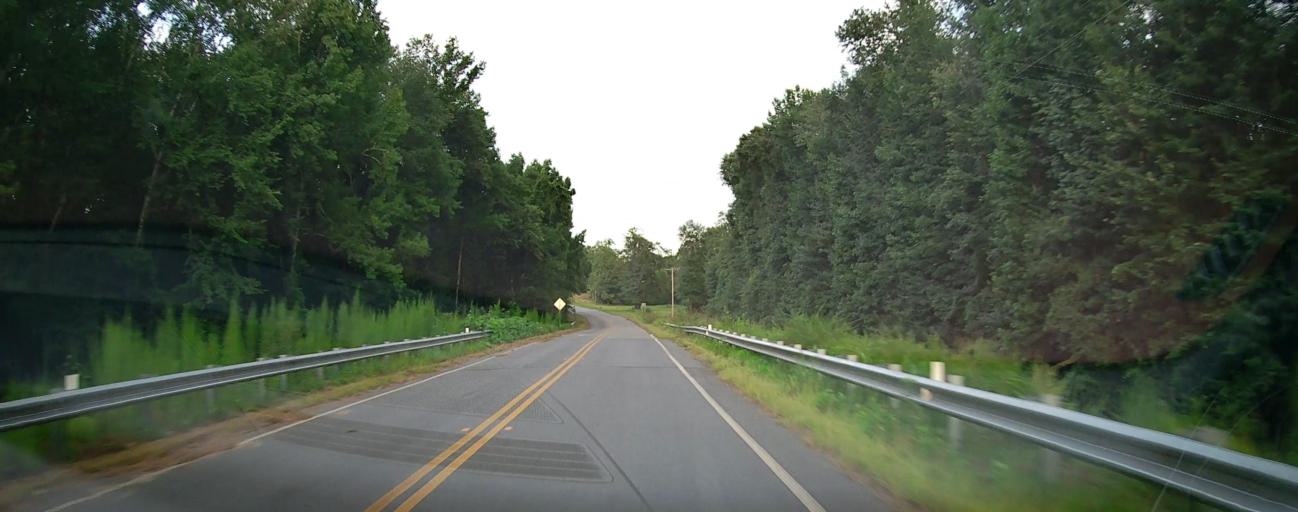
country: US
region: Georgia
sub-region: Crawford County
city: Roberta
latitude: 32.6525
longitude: -84.0319
